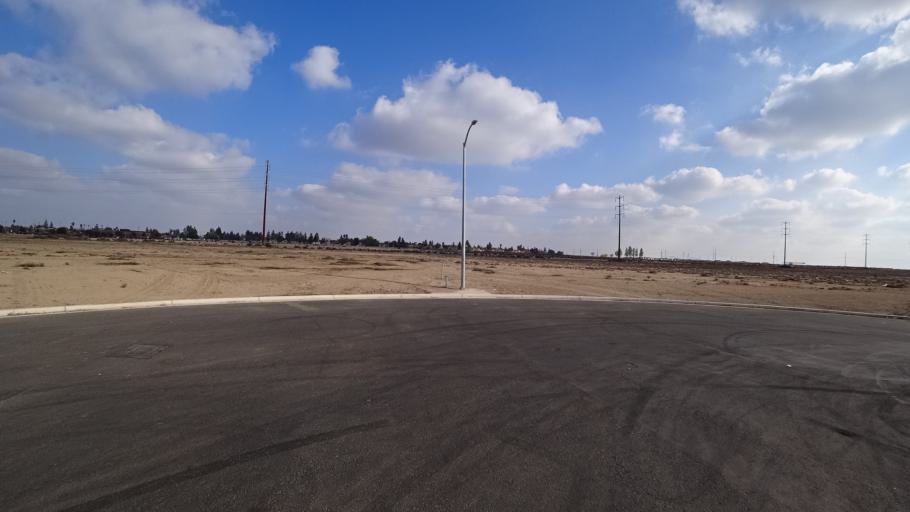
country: US
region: California
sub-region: Kern County
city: Greenacres
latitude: 35.3016
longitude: -119.0976
